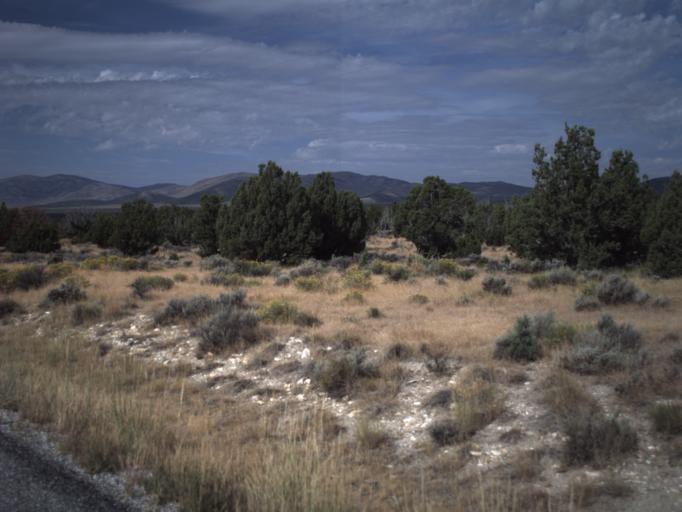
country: US
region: Idaho
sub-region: Cassia County
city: Burley
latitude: 41.8061
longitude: -113.4495
